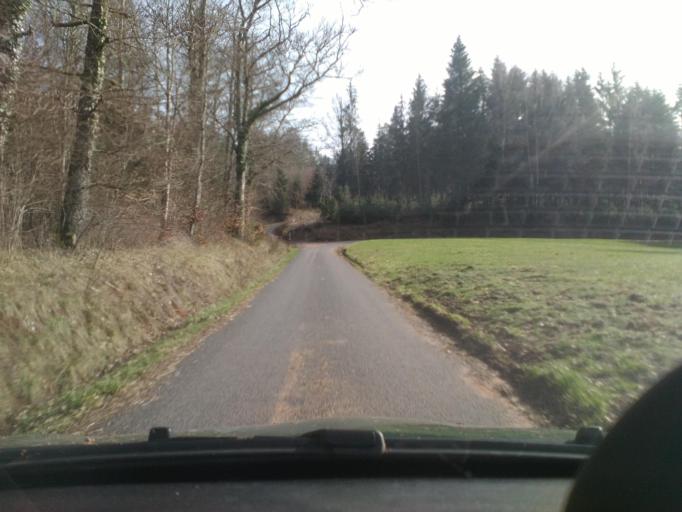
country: FR
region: Lorraine
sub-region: Departement des Vosges
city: Saint-Michel-sur-Meurthe
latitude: 48.3354
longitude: 6.9282
